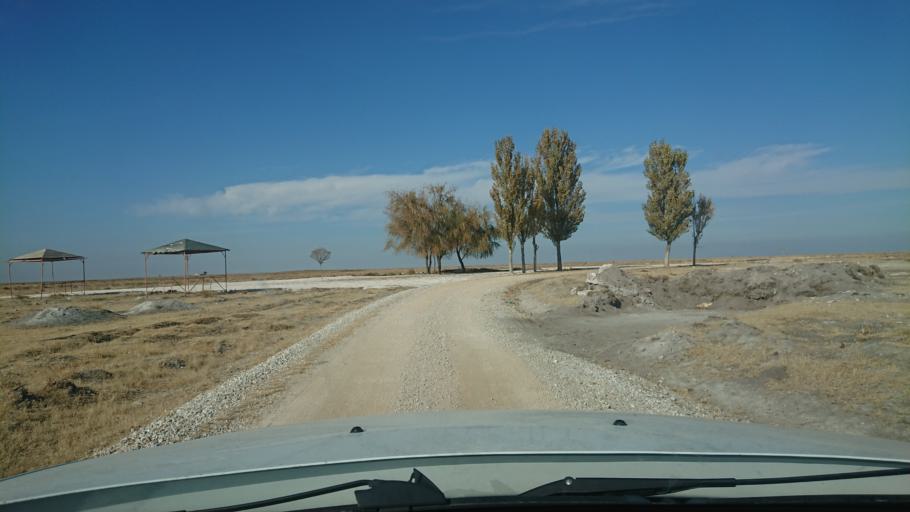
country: TR
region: Aksaray
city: Eskil
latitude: 38.4744
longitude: 33.4577
